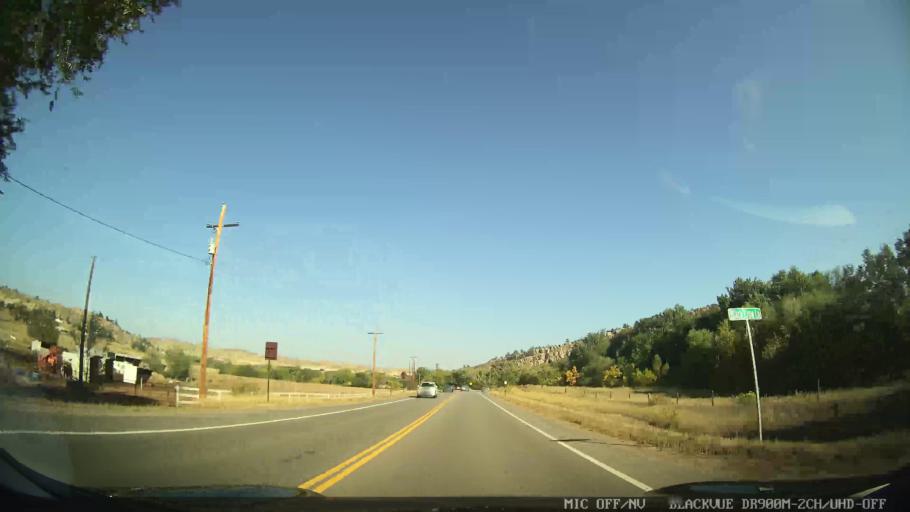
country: US
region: Colorado
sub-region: Larimer County
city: Loveland
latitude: 40.4180
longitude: -105.1859
